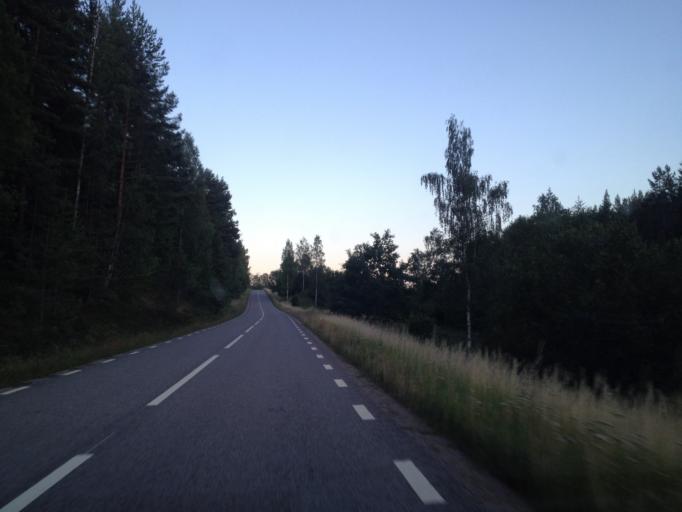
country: SE
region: Kalmar
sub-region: Vasterviks Kommun
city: Overum
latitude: 58.0037
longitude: 16.1742
